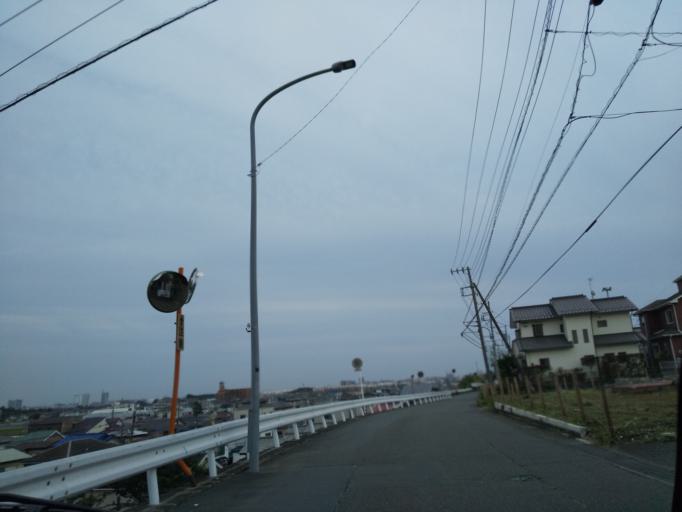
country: JP
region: Kanagawa
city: Atsugi
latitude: 35.4727
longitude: 139.3532
